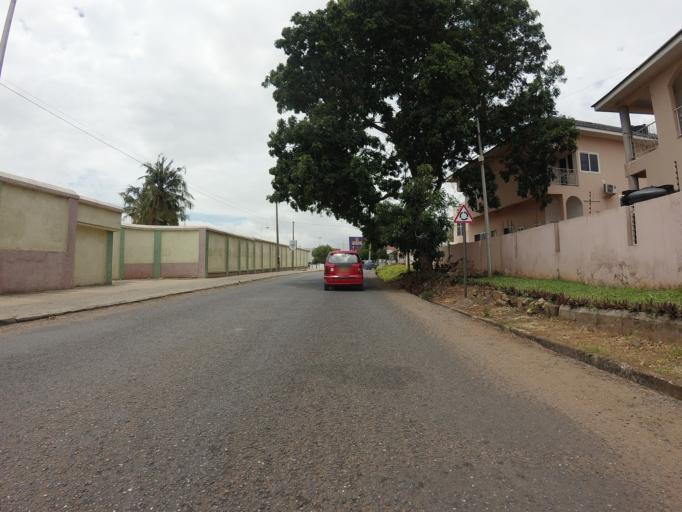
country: GH
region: Greater Accra
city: Accra
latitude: 5.5762
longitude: -0.1778
